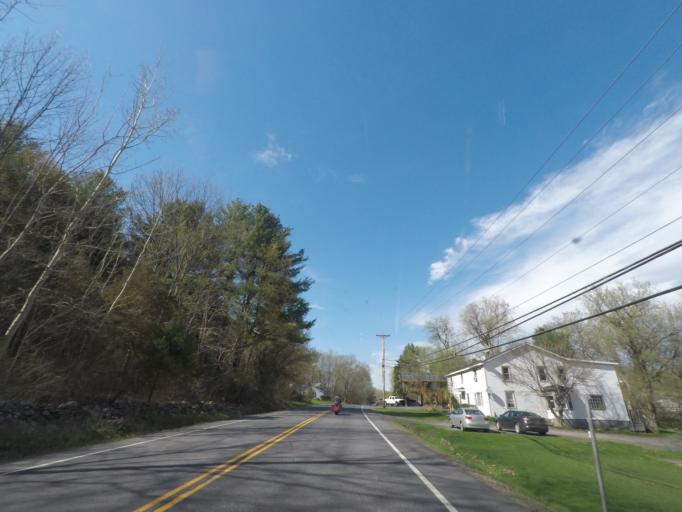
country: US
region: New York
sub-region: Greene County
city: Cairo
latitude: 42.3554
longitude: -74.0486
